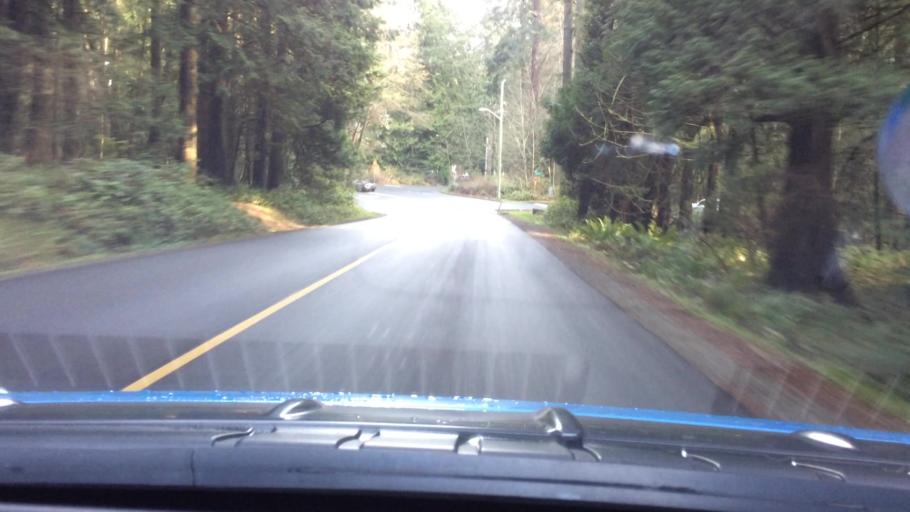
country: CA
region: British Columbia
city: Oak Bay
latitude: 48.4941
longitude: -123.3357
